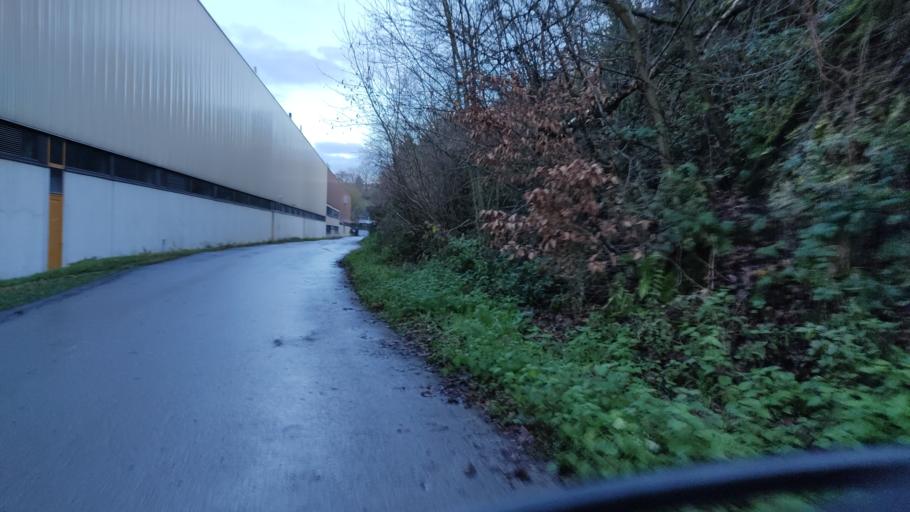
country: DE
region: North Rhine-Westphalia
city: Hattingen
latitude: 51.3746
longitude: 7.1262
